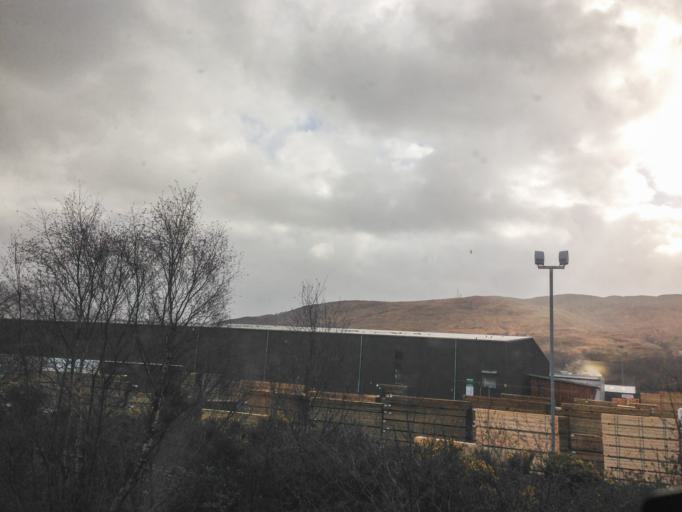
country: GB
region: Scotland
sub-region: Highland
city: Fort William
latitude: 56.8429
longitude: -5.1479
